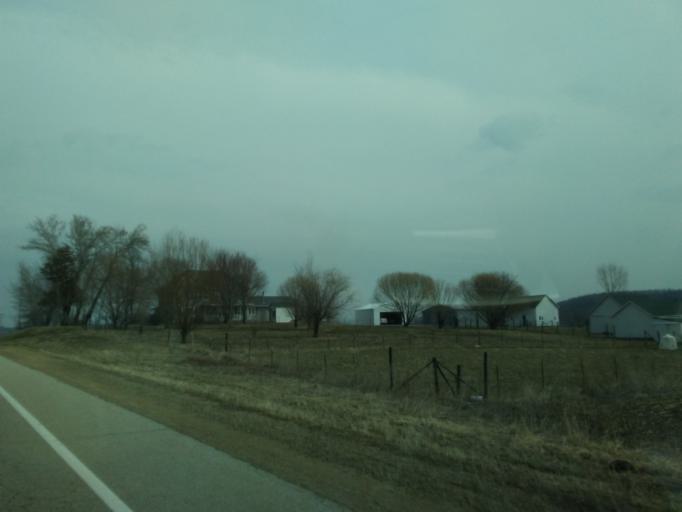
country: US
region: Wisconsin
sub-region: Columbia County
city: Lodi
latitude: 43.2814
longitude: -89.5214
